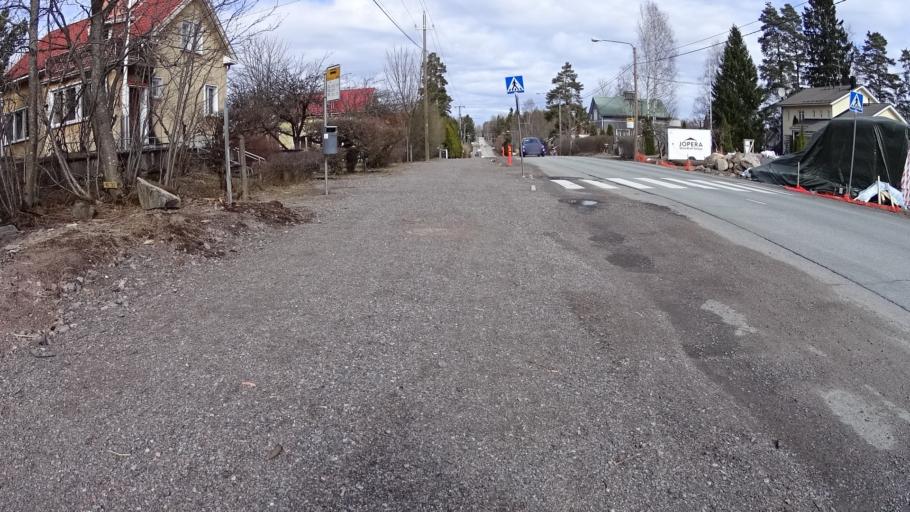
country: FI
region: Uusimaa
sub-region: Helsinki
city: Kilo
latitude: 60.2392
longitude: 24.8086
